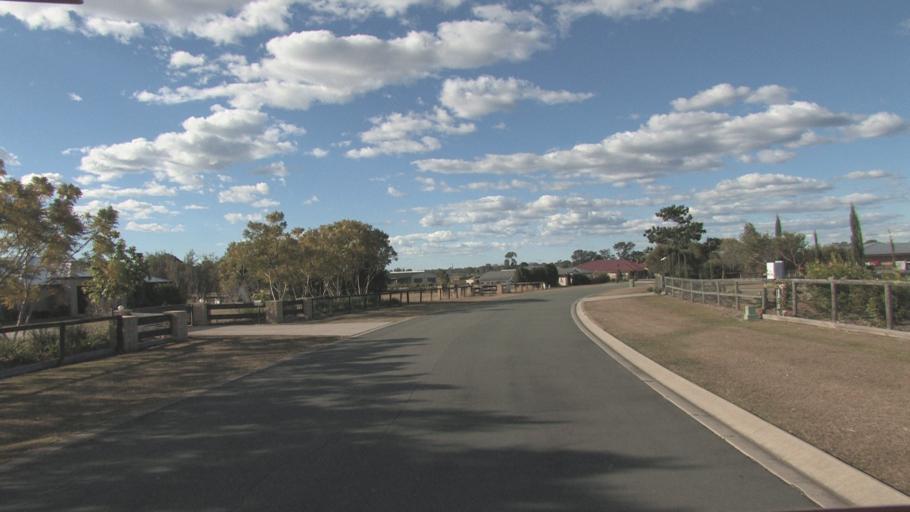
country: AU
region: Queensland
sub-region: Logan
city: North Maclean
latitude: -27.8259
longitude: 153.0029
